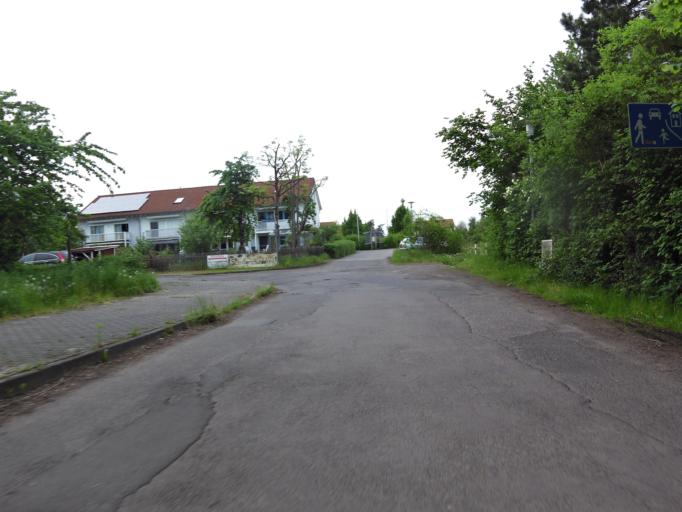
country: DE
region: Saxony
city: Zwenkau
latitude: 51.2744
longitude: 12.3056
